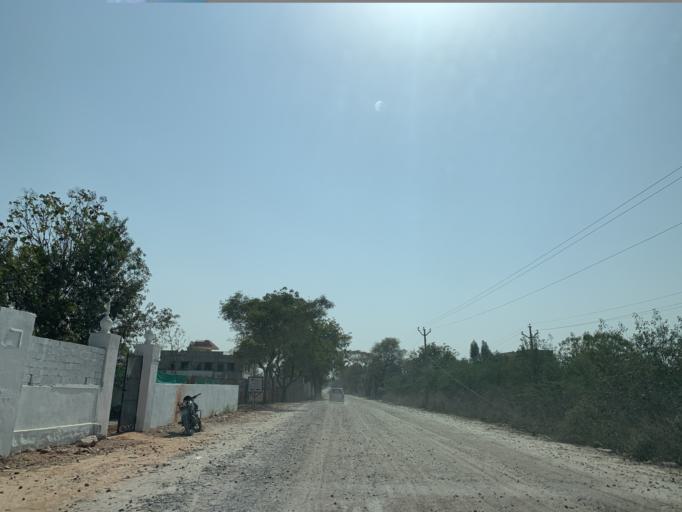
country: IN
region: Telangana
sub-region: Rangareddi
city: Sriramnagar
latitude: 17.3276
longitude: 78.2953
